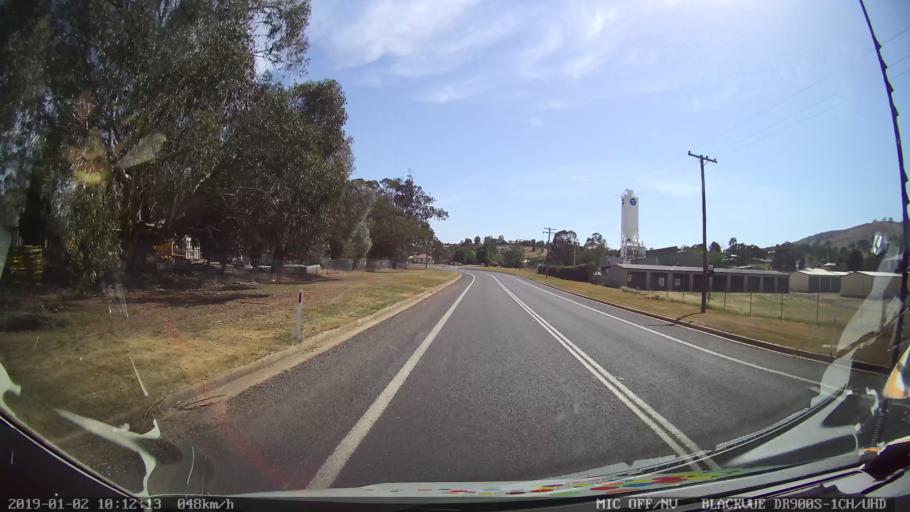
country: AU
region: New South Wales
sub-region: Gundagai
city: Gundagai
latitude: -35.0861
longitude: 148.0945
